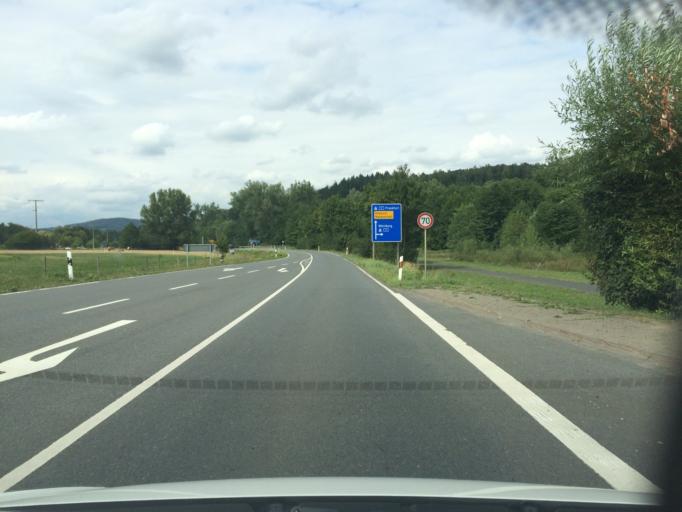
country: DE
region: Bavaria
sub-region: Regierungsbezirk Unterfranken
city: Sailauf
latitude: 49.9836
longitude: 9.2550
